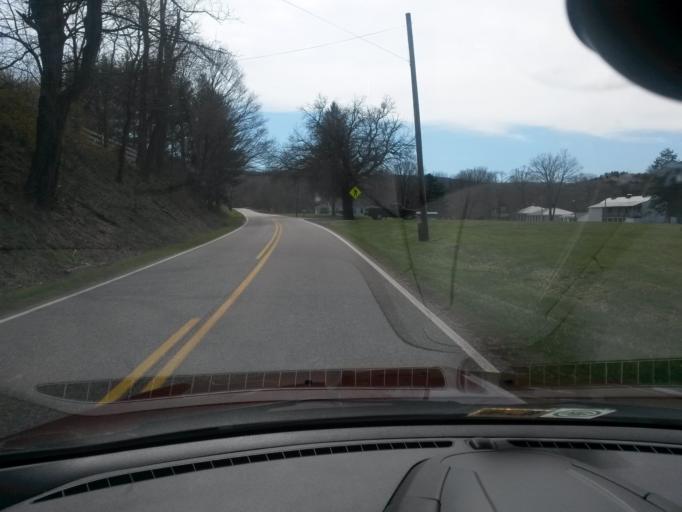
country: US
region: West Virginia
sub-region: Greenbrier County
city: White Sulphur Springs
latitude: 37.6456
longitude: -80.2377
